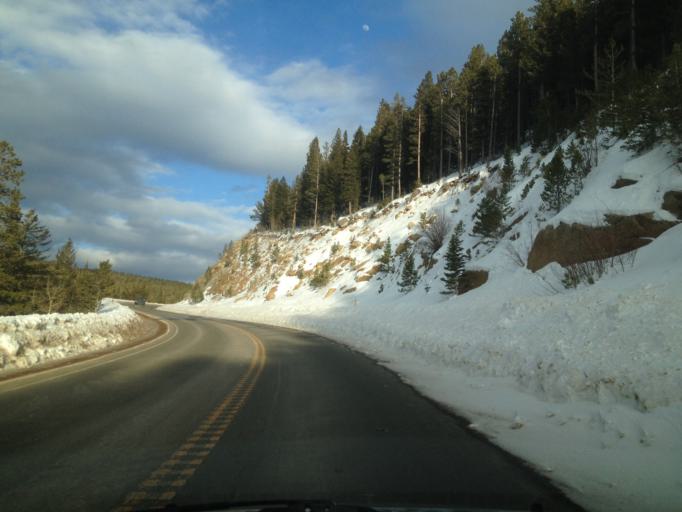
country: US
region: Colorado
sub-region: Boulder County
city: Nederland
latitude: 40.1301
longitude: -105.4965
